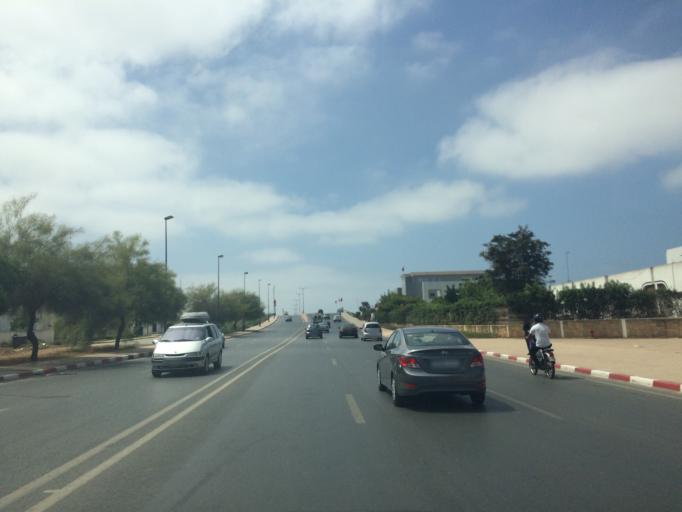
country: MA
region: Rabat-Sale-Zemmour-Zaer
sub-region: Skhirate-Temara
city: Temara
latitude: 33.9704
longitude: -6.8765
